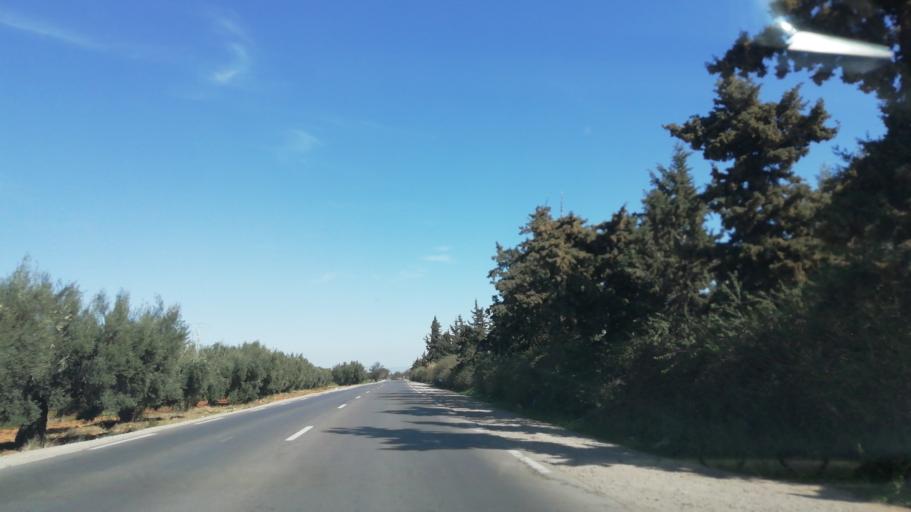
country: DZ
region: Mascara
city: Oued el Abtal
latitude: 35.4257
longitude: 0.4568
